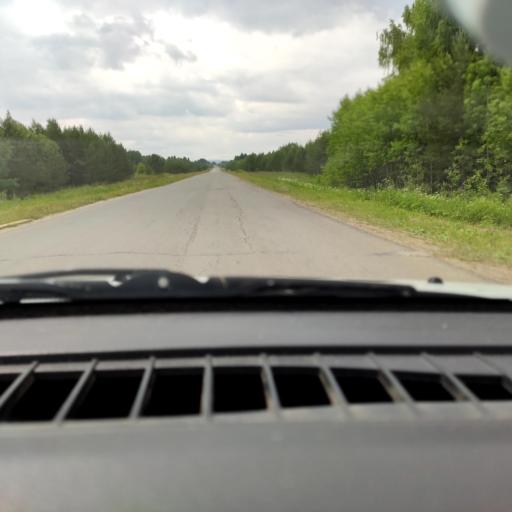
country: RU
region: Perm
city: Orda
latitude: 57.1196
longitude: 56.6736
